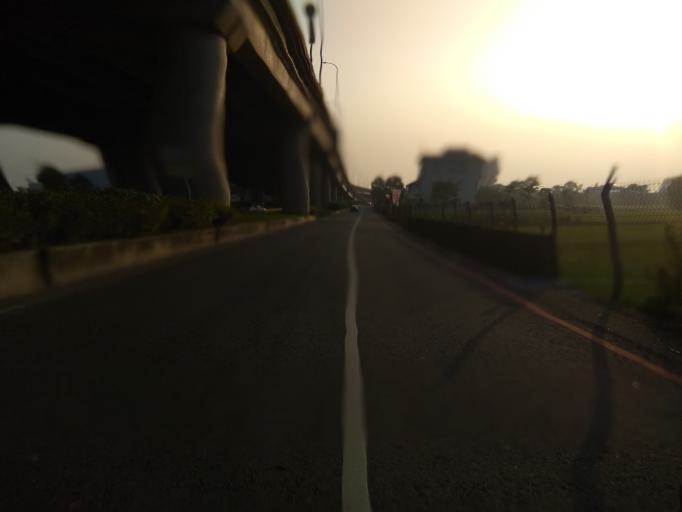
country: TW
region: Taiwan
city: Daxi
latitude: 24.9283
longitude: 121.2090
